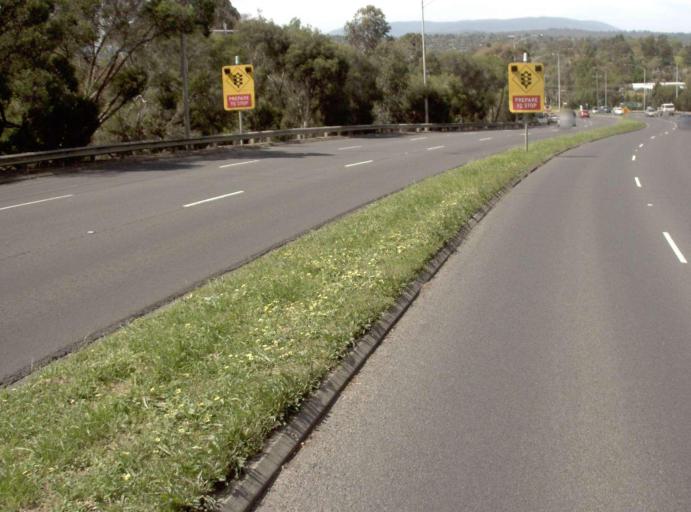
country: AU
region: Victoria
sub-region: Maroondah
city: Croydon Hills
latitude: -37.7837
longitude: 145.2807
